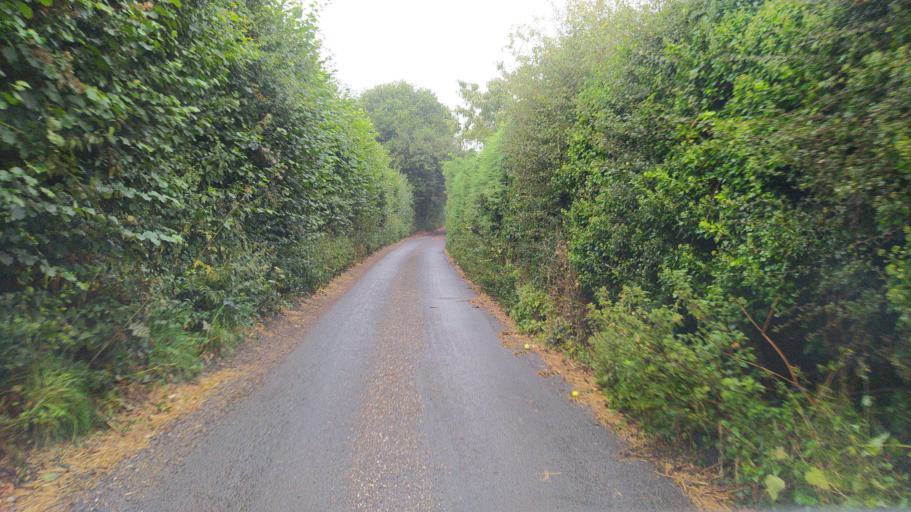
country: GB
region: England
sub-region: Wiltshire
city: Ansty
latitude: 51.0109
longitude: -2.1104
